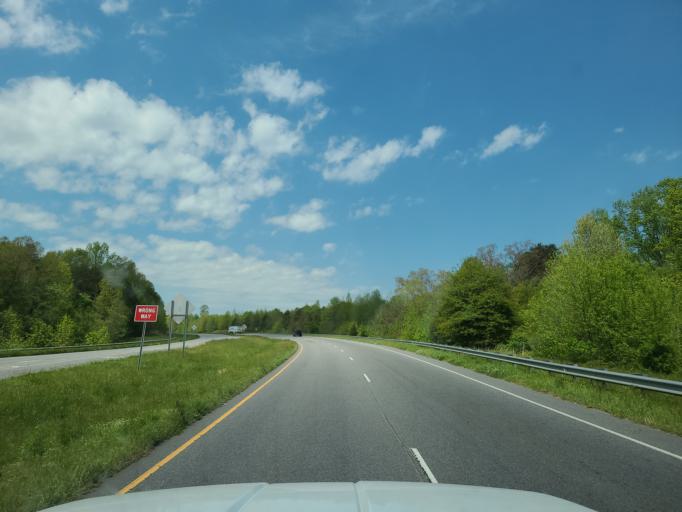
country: US
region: North Carolina
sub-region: Lincoln County
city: Lincolnton
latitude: 35.4267
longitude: -81.3045
